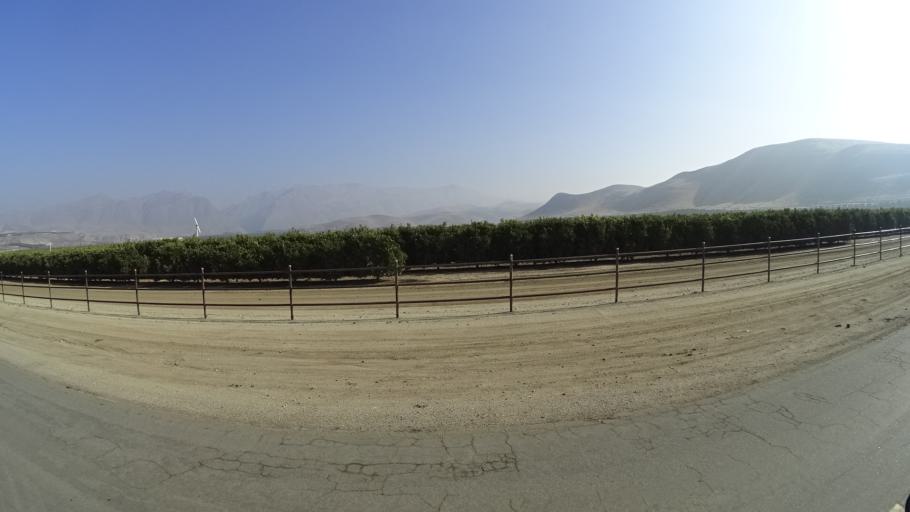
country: US
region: California
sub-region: Kern County
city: Lamont
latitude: 35.4192
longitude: -118.8326
